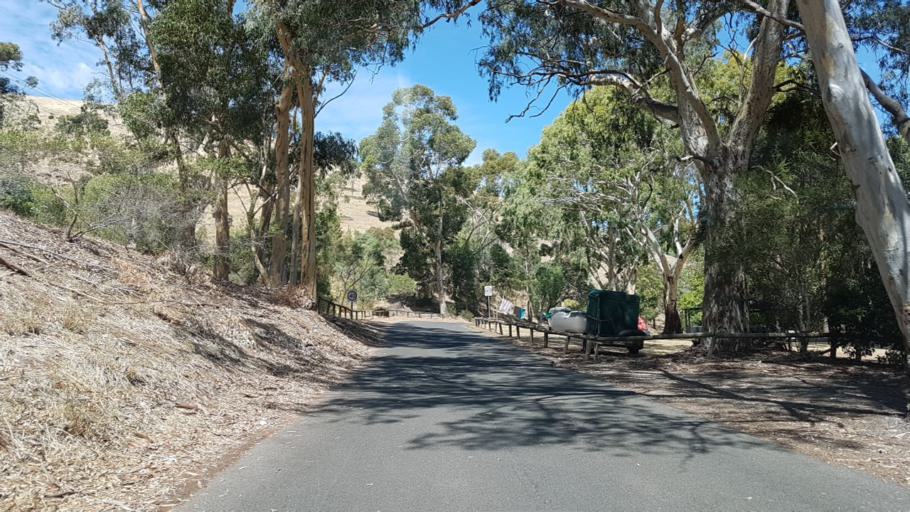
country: AU
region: South Australia
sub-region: Mitcham
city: Mitcham
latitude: -34.9859
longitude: 138.6277
